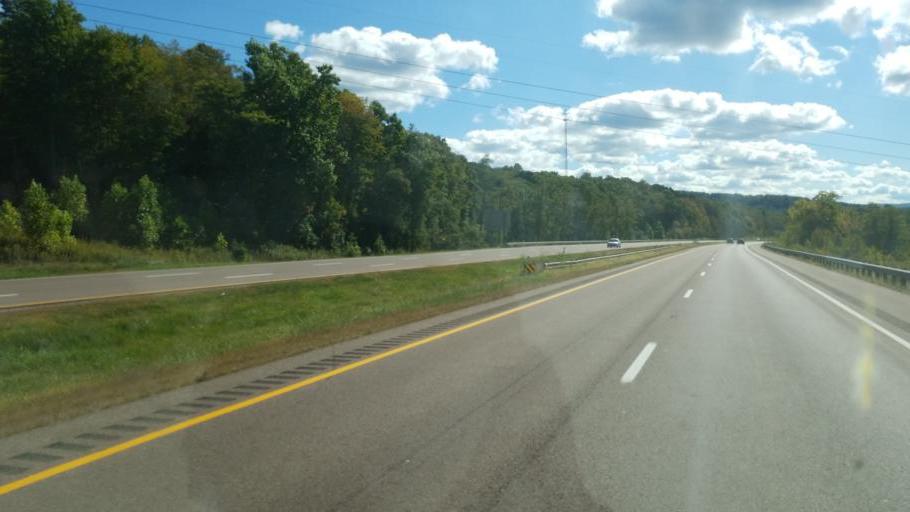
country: US
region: Maryland
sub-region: Garrett County
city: Oakland
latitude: 39.6729
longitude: -79.3842
